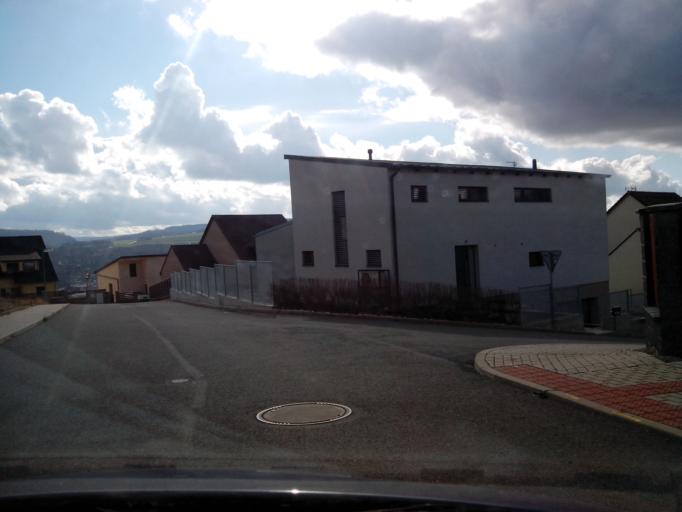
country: CZ
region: Central Bohemia
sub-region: Okres Beroun
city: Kraluv Dvur
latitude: 49.9552
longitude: 14.0383
